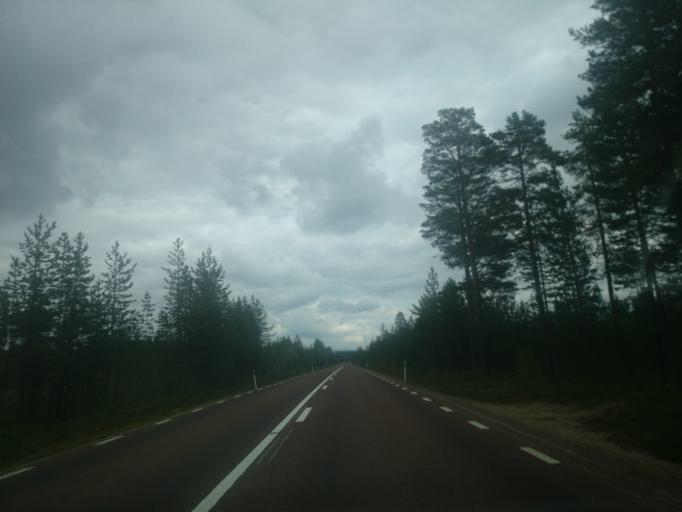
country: SE
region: Jaemtland
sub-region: Harjedalens Kommun
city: Sveg
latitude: 62.0531
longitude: 14.5297
